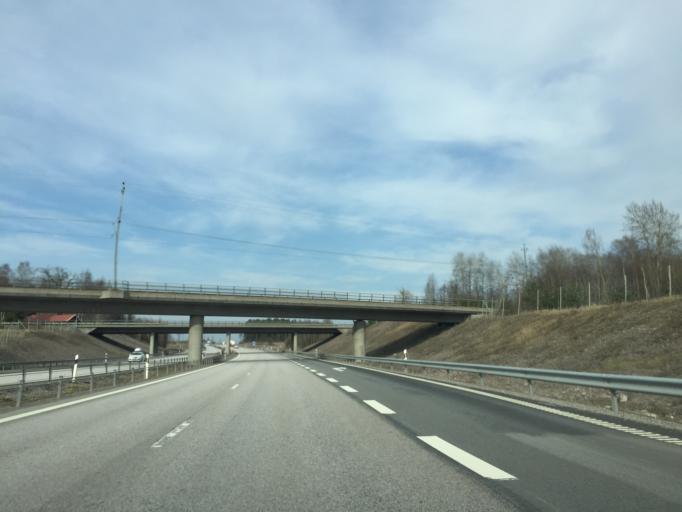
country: SE
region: Vaestmanland
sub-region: Arboga Kommun
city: Arboga
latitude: 59.4111
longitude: 15.7675
